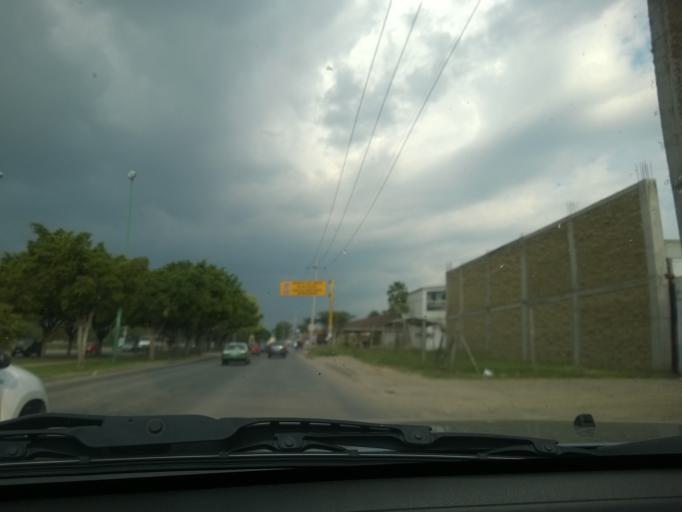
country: MX
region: Guanajuato
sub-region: Leon
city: Medina
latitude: 21.1260
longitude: -101.6354
